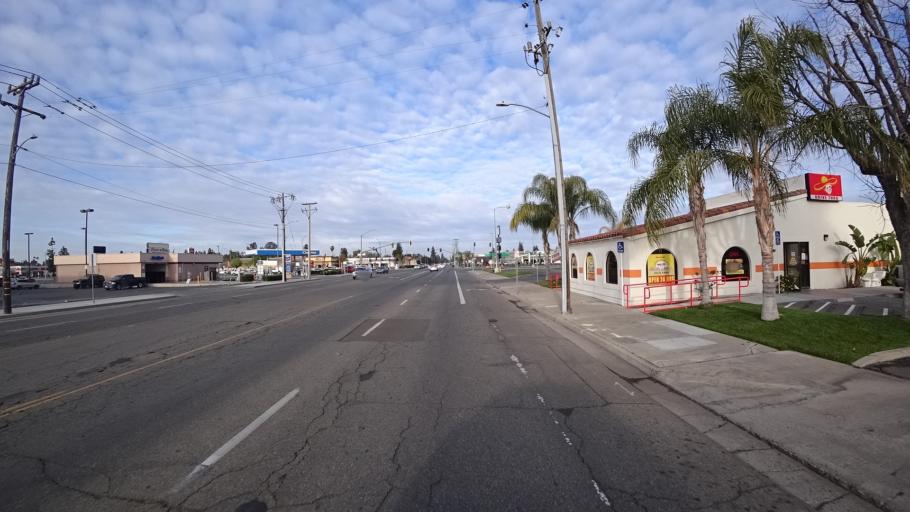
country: US
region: California
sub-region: Fresno County
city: Fresno
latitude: 36.8158
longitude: -119.7893
